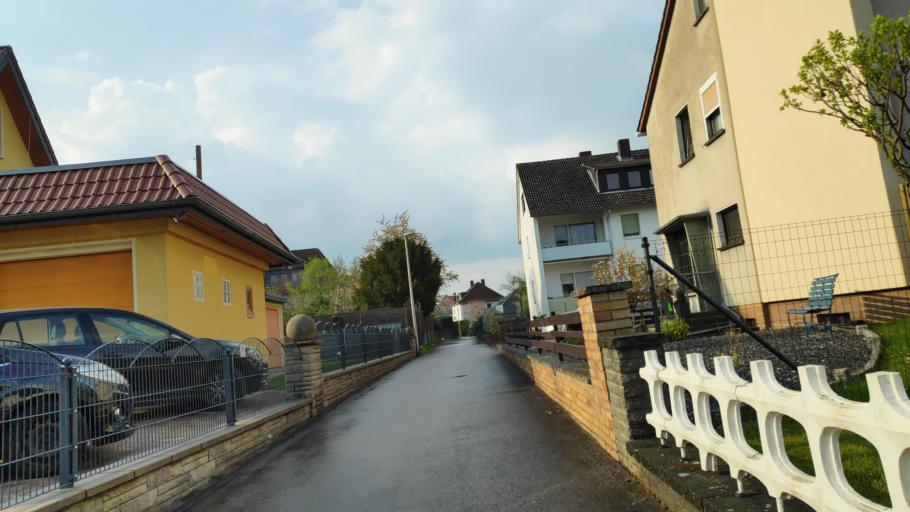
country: DE
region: North Rhine-Westphalia
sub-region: Regierungsbezirk Detmold
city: Minden
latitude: 52.2894
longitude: 8.9476
